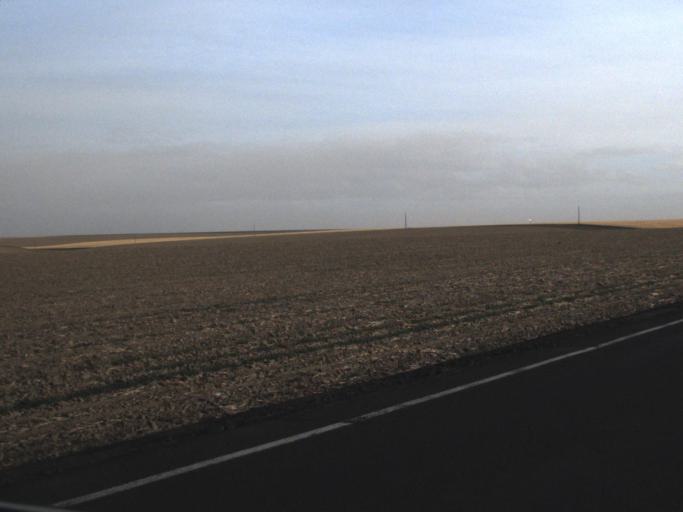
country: US
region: Washington
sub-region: Adams County
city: Ritzville
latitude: 47.2114
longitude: -118.6863
